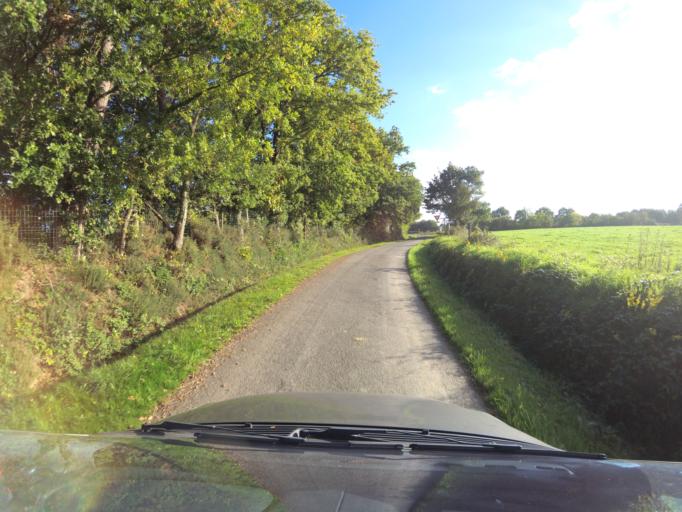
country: FR
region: Brittany
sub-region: Departement du Morbihan
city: Peillac
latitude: 47.7156
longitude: -2.1949
